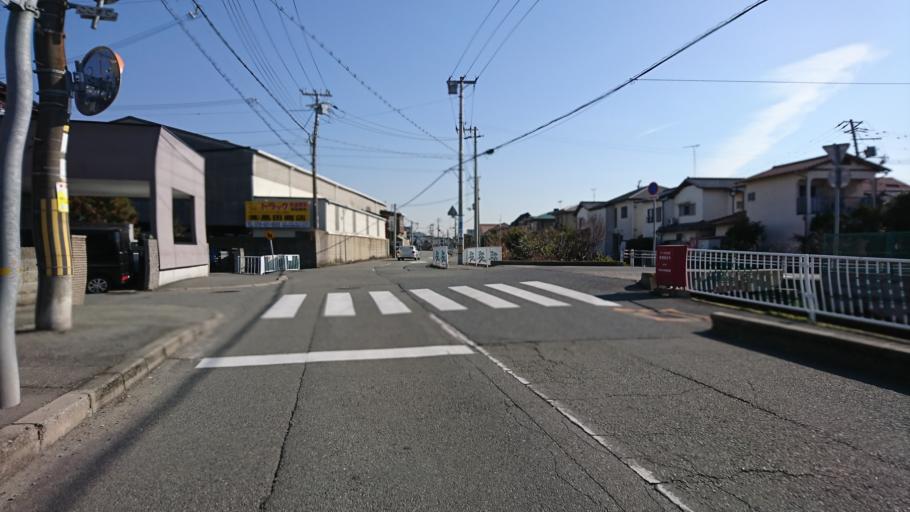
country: JP
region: Hyogo
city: Kakogawacho-honmachi
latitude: 34.7768
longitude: 134.8182
